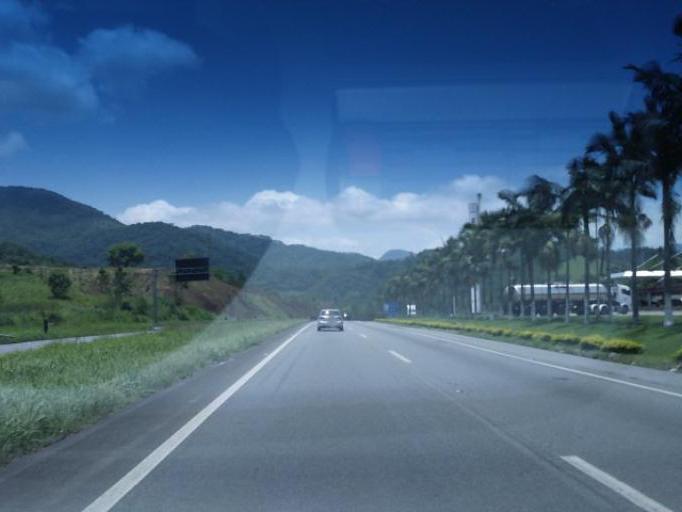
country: BR
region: Sao Paulo
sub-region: Miracatu
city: Miracatu
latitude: -24.2584
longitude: -47.3767
